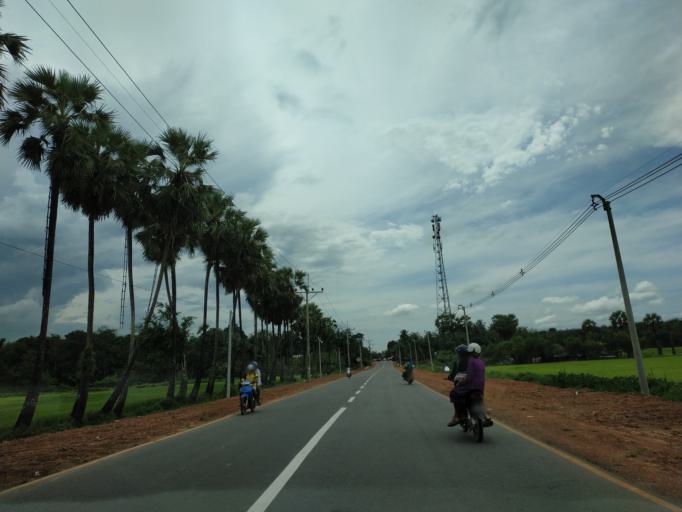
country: MM
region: Tanintharyi
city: Dawei
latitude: 14.0452
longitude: 98.2214
